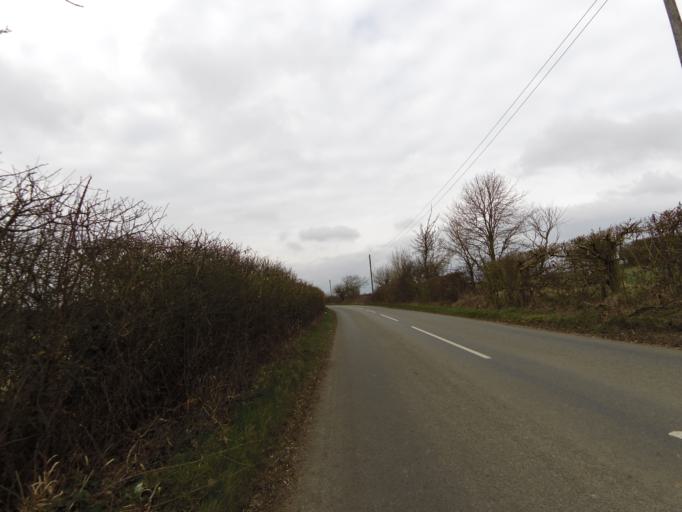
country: GB
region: England
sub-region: Suffolk
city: Beccles
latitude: 52.4043
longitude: 1.5358
